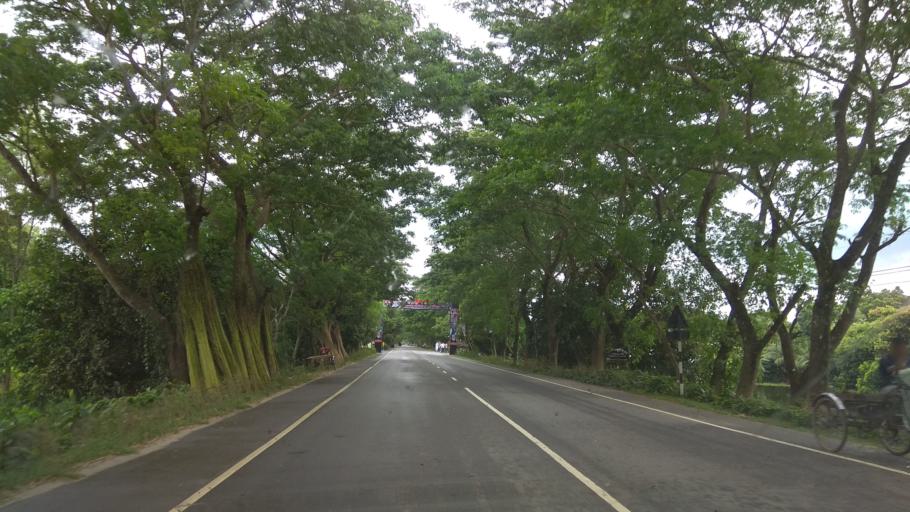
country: BD
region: Khulna
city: Kalia
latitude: 23.2419
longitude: 89.7521
